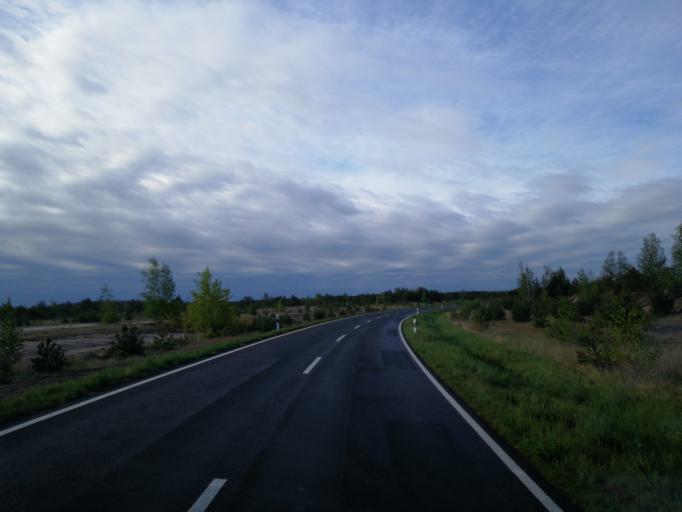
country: DE
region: Brandenburg
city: Sallgast
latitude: 51.5672
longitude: 13.7791
